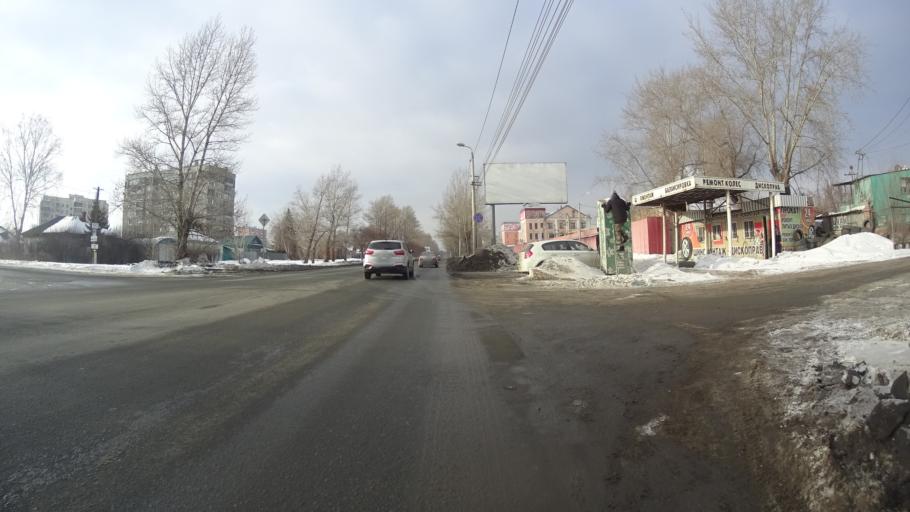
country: RU
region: Chelyabinsk
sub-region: Gorod Chelyabinsk
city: Chelyabinsk
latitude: 55.1222
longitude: 61.3764
